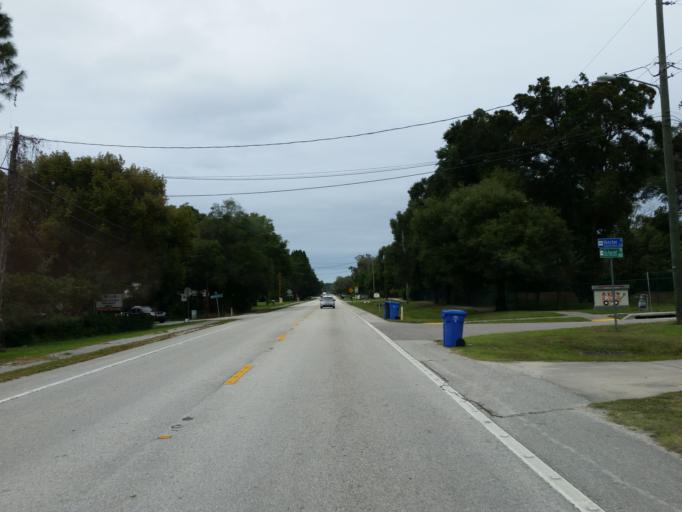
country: US
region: Florida
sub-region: Hillsborough County
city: Bloomingdale
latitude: 27.9154
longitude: -82.2630
